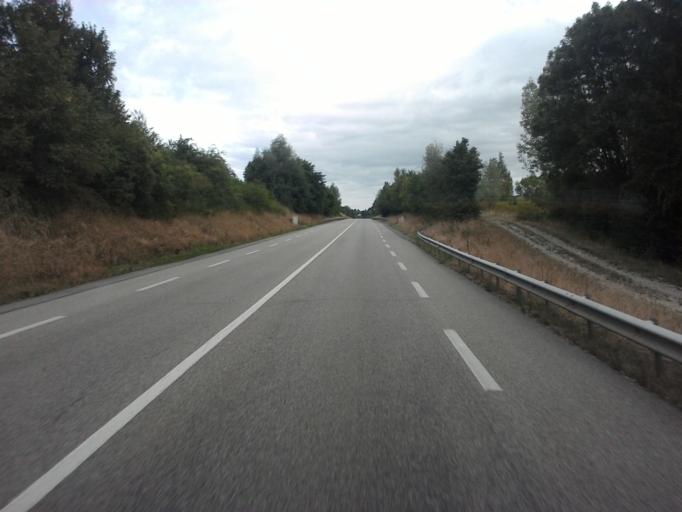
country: FR
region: Rhone-Alpes
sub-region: Departement de l'Ain
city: Lagnieu
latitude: 45.8989
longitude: 5.3376
